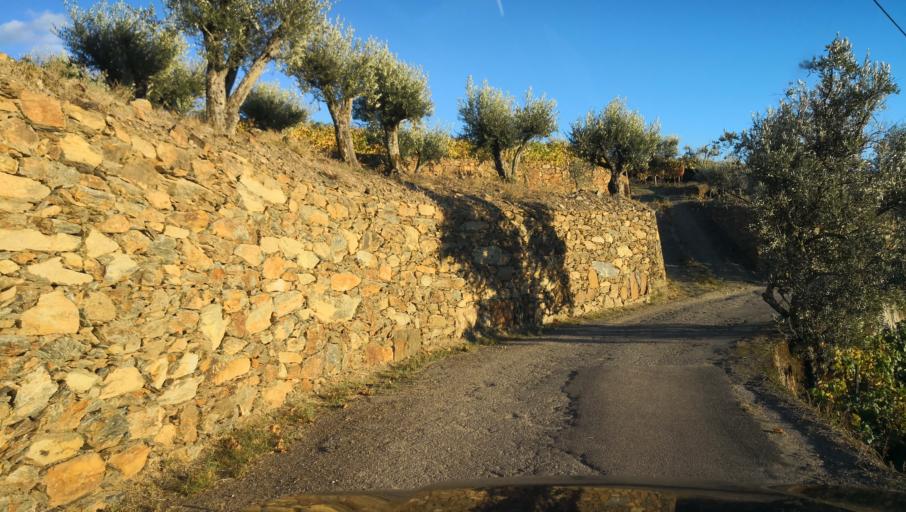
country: PT
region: Vila Real
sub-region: Santa Marta de Penaguiao
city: Santa Marta de Penaguiao
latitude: 41.2489
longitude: -7.7674
